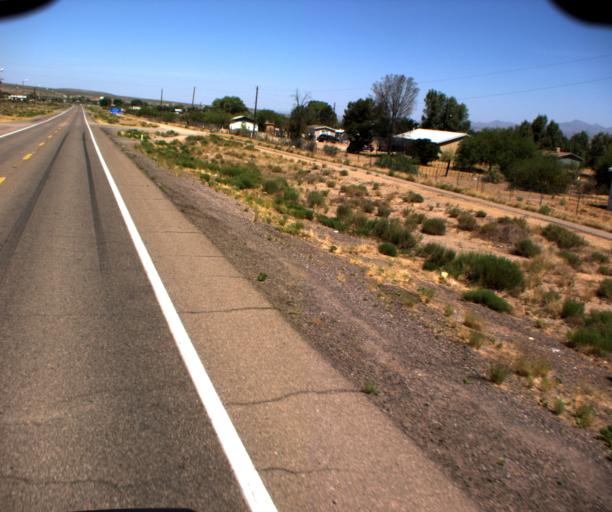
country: US
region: Arizona
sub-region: Graham County
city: Bylas
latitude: 33.1114
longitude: -110.0949
